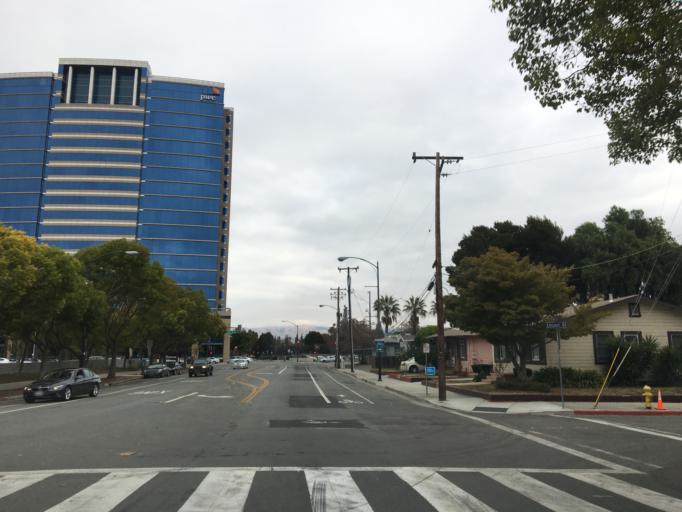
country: US
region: California
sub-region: Santa Clara County
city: San Jose
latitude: 37.3259
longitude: -121.8904
